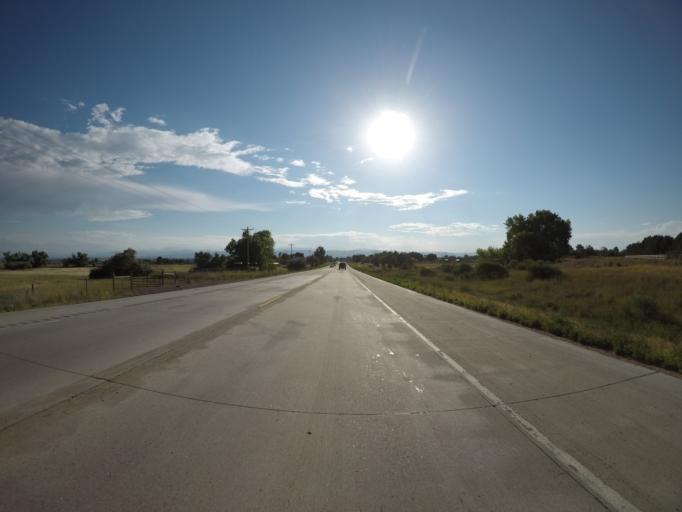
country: US
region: Colorado
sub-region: Weld County
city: Severance
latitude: 40.5816
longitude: -104.9174
